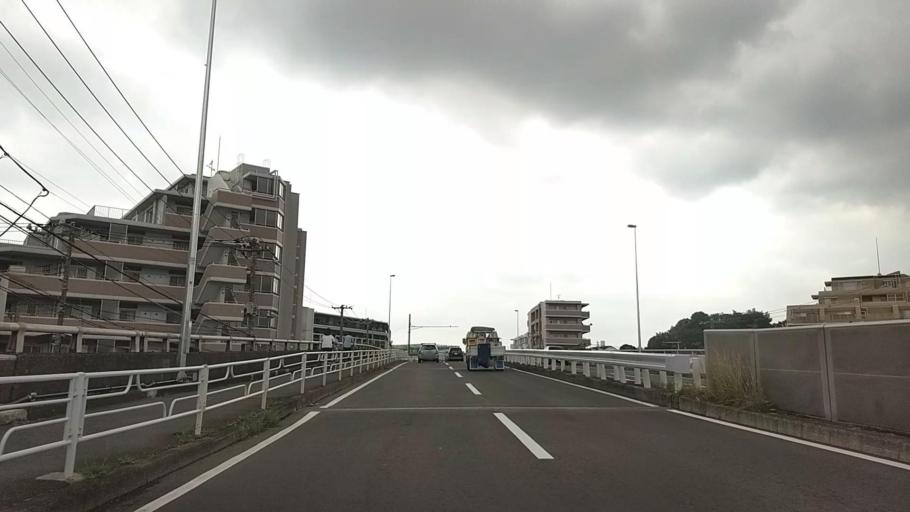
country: JP
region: Kanagawa
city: Yokohama
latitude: 35.4943
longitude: 139.6074
